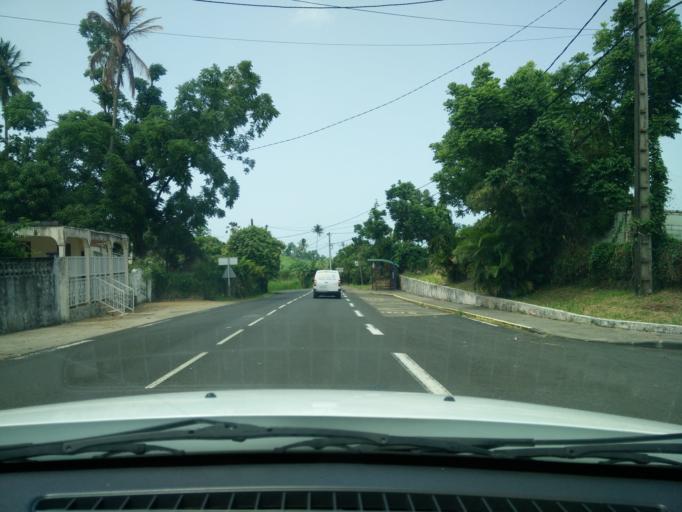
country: GP
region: Guadeloupe
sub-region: Guadeloupe
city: Trois-Rivieres
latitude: 15.9770
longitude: -61.6372
